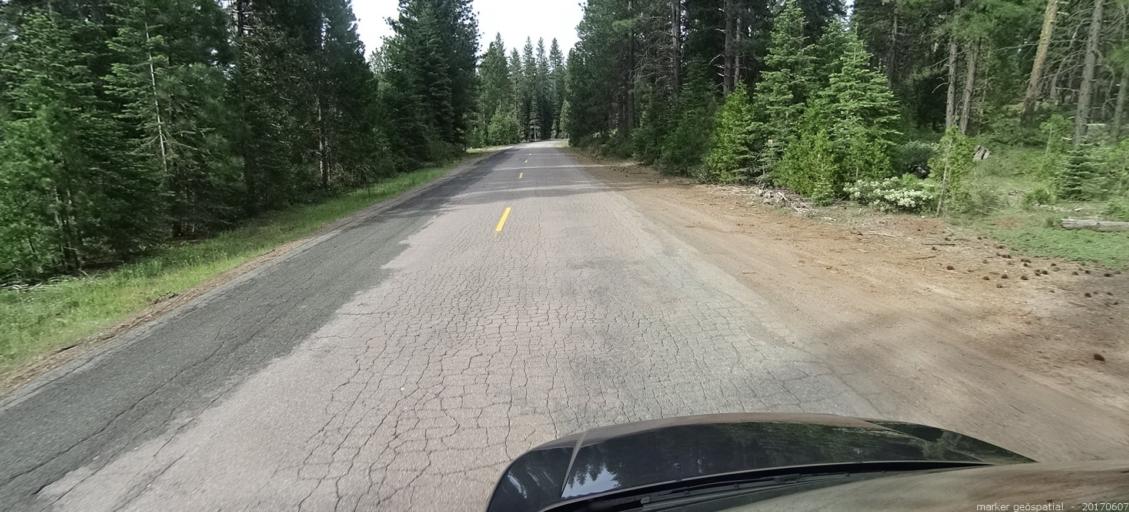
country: US
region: California
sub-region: Shasta County
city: Burney
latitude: 41.1814
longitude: -121.7080
